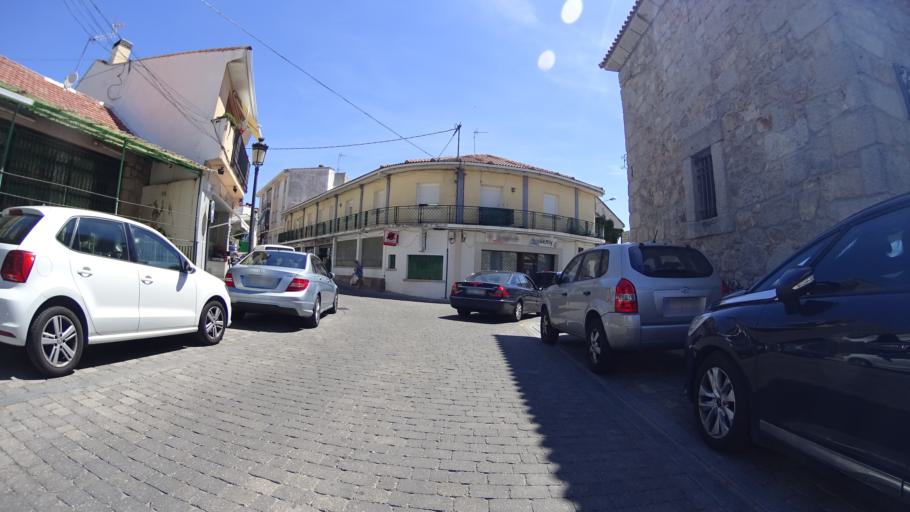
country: ES
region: Madrid
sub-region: Provincia de Madrid
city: Hoyo de Manzanares
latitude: 40.6226
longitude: -3.9067
